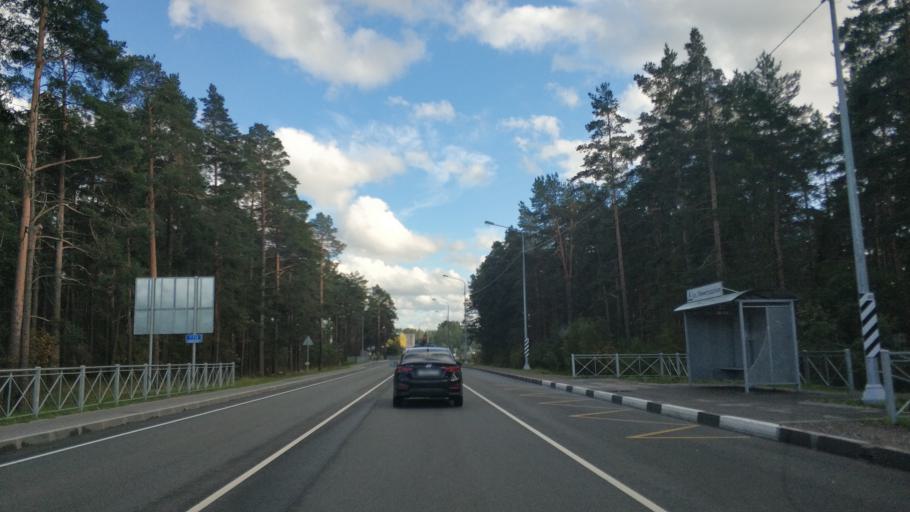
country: RU
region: Leningrad
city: Priozersk
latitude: 61.0046
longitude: 30.1798
